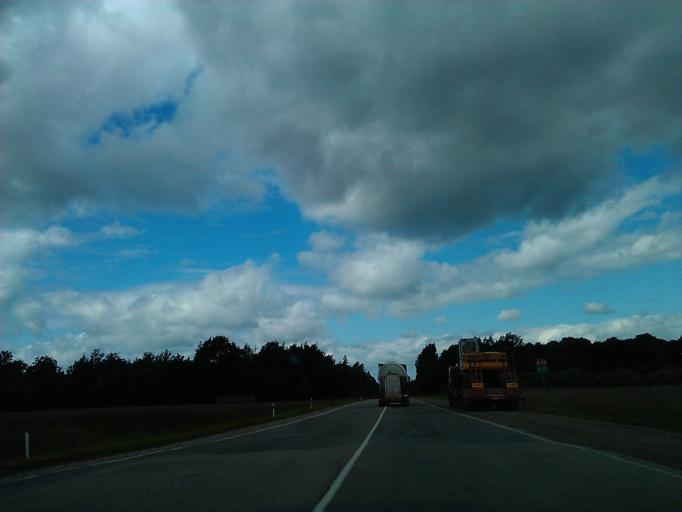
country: LV
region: Tukuma Rajons
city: Tukums
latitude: 56.9331
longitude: 23.1997
